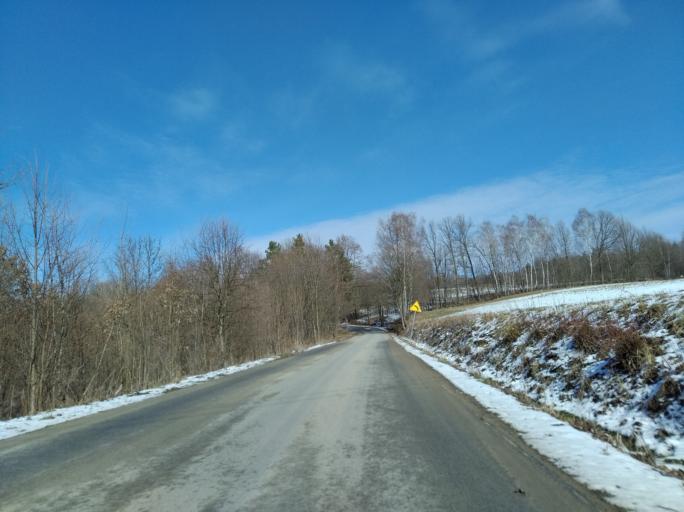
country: PL
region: Subcarpathian Voivodeship
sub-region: Powiat brzozowski
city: Jablonica Polska
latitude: 49.7178
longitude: 21.8800
